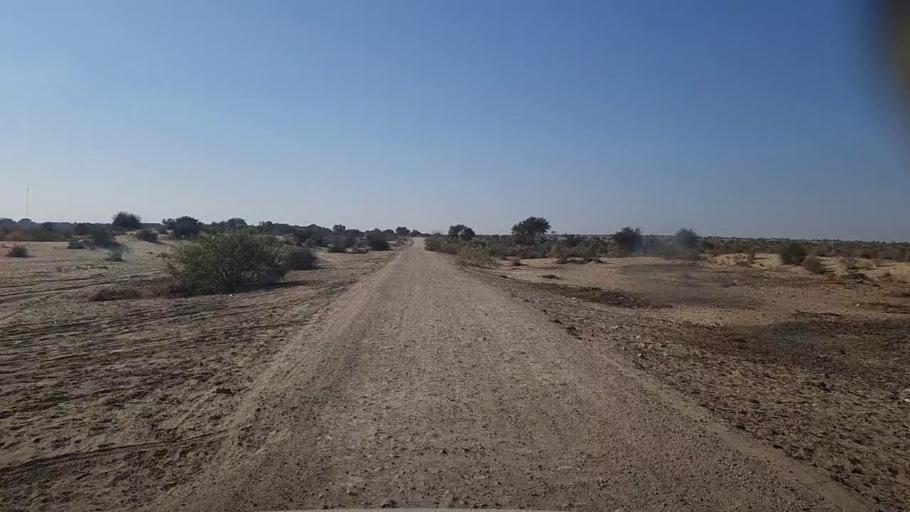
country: PK
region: Sindh
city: Khairpur
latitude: 27.9586
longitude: 69.8368
